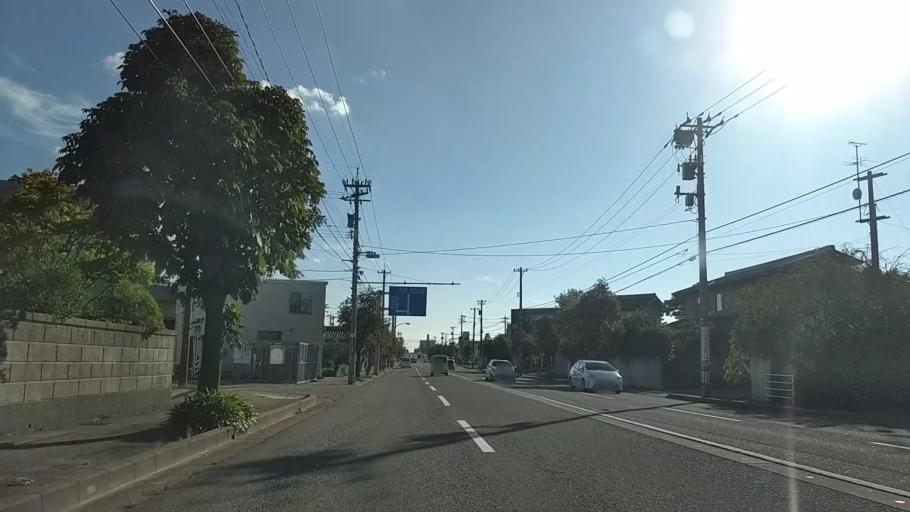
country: JP
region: Ishikawa
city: Kanazawa-shi
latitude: 36.5767
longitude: 136.6342
